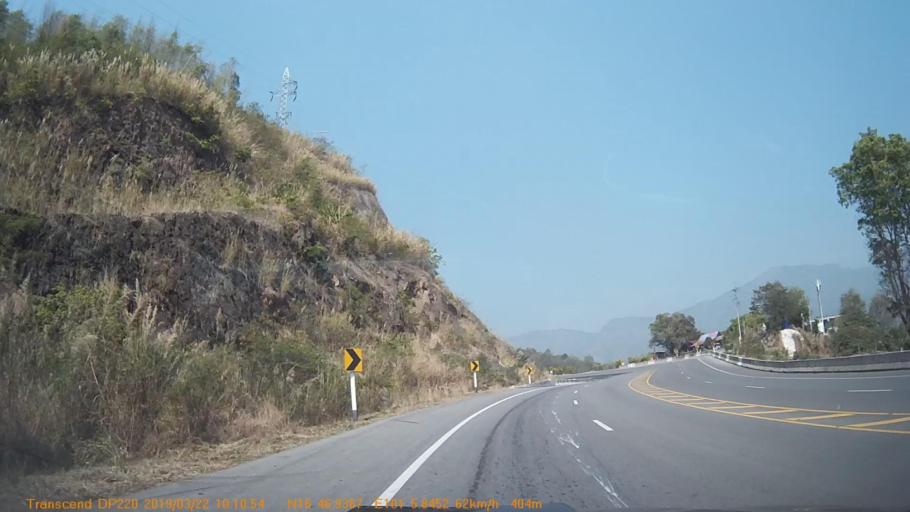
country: TH
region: Phetchabun
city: Lom Sak
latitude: 16.7823
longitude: 101.0972
